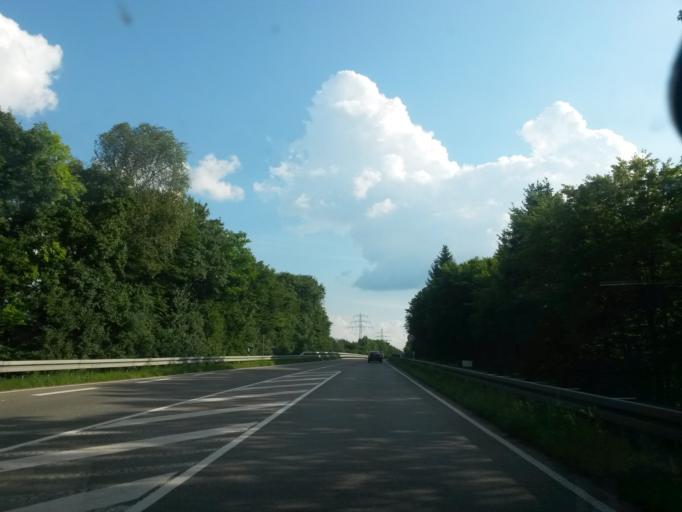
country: DE
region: Bavaria
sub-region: Upper Bavaria
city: Putzbrunn
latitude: 48.0652
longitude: 11.7114
